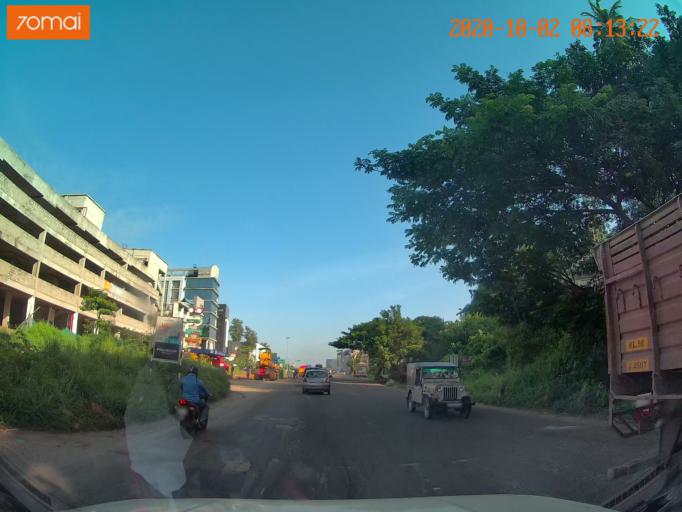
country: IN
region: Kerala
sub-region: Kozhikode
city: Kozhikode
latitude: 11.2858
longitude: 75.8015
